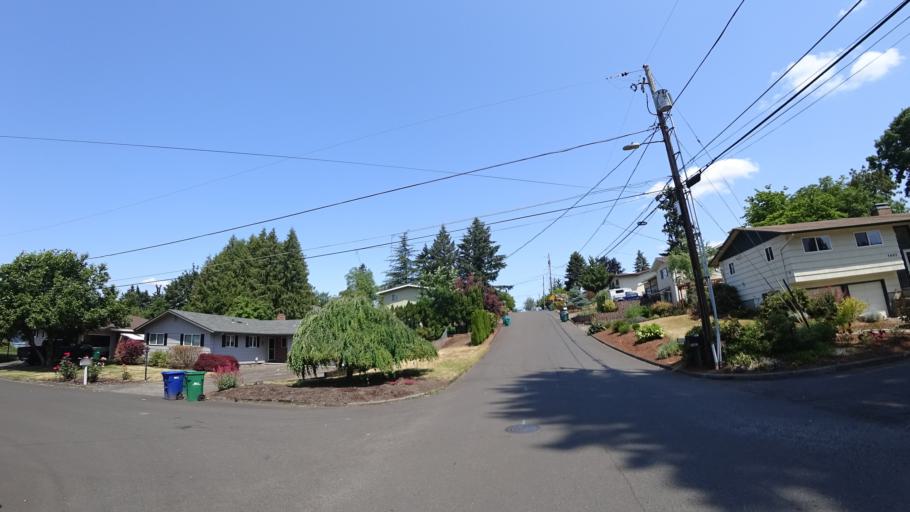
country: US
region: Oregon
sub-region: Clackamas County
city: Oatfield
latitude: 45.4453
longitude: -122.5872
